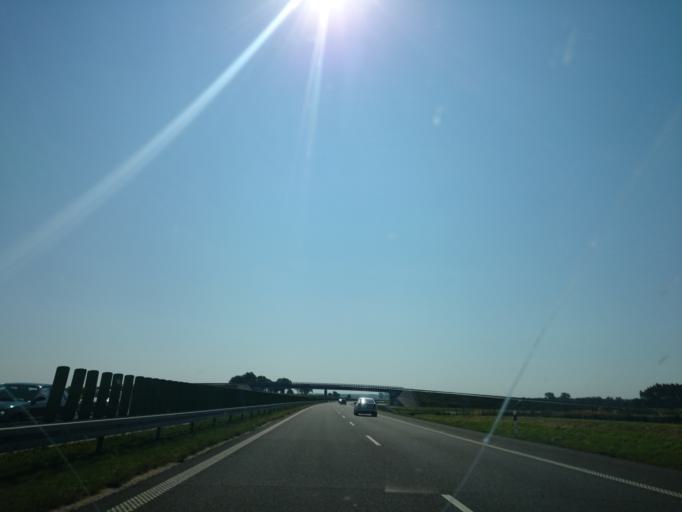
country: PL
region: West Pomeranian Voivodeship
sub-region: Powiat pyrzycki
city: Bielice
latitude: 53.2073
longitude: 14.6722
